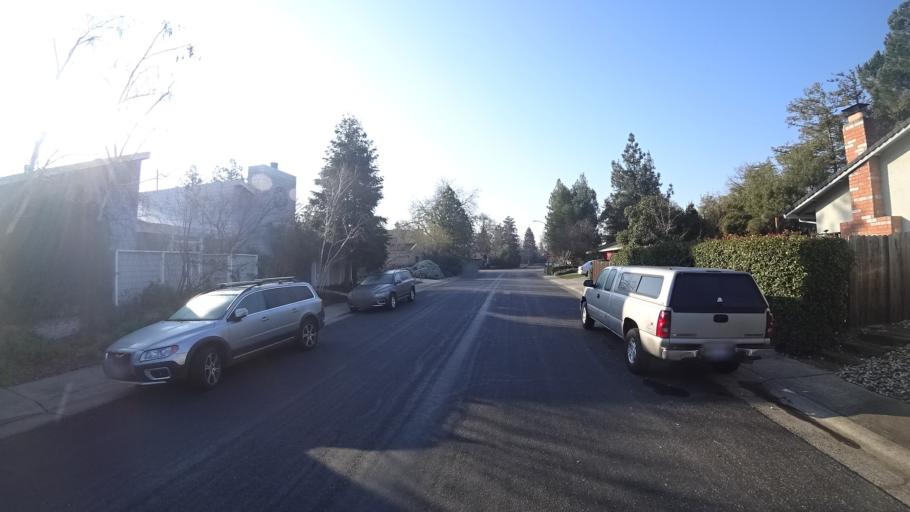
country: US
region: California
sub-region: Yolo County
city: Davis
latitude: 38.5569
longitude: -121.7898
